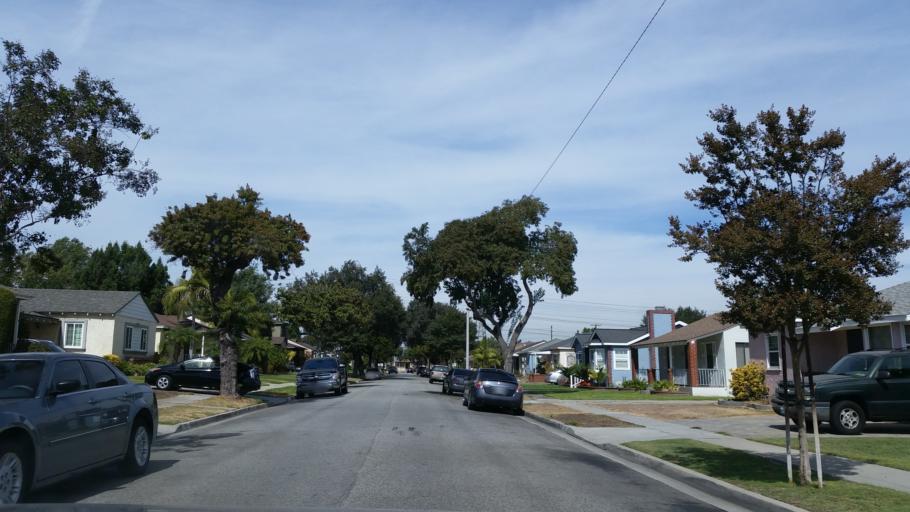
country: US
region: California
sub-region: Los Angeles County
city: Lakewood
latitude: 33.8657
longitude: -118.1318
